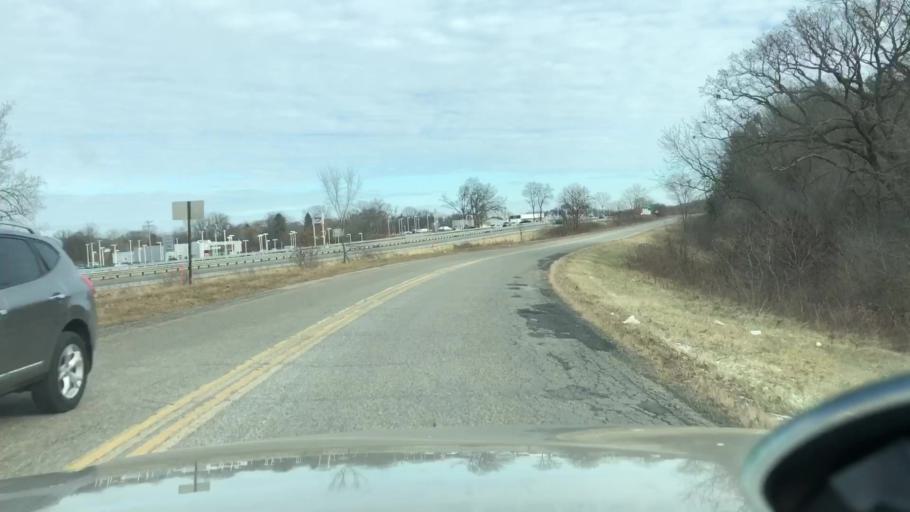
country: US
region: Michigan
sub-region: Jackson County
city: Jackson
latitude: 42.2755
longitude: -84.3791
